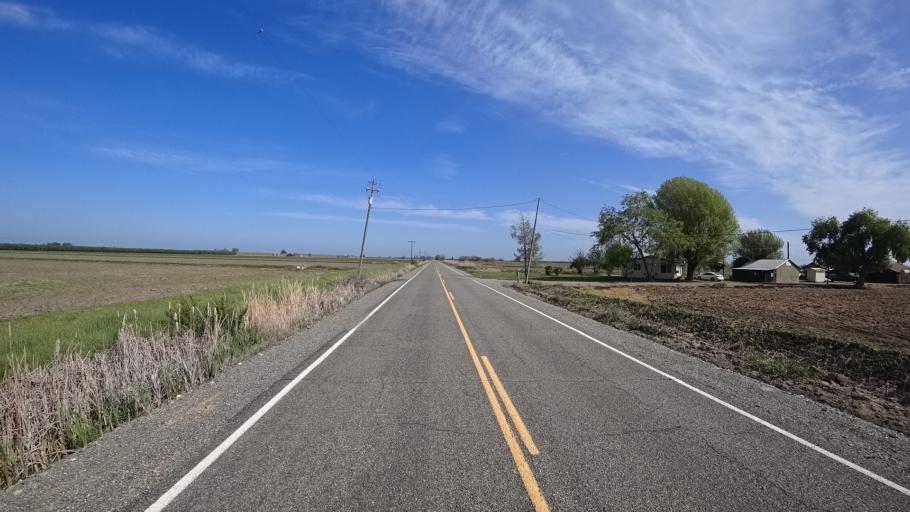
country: US
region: California
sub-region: Glenn County
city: Hamilton City
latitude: 39.6091
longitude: -122.0369
